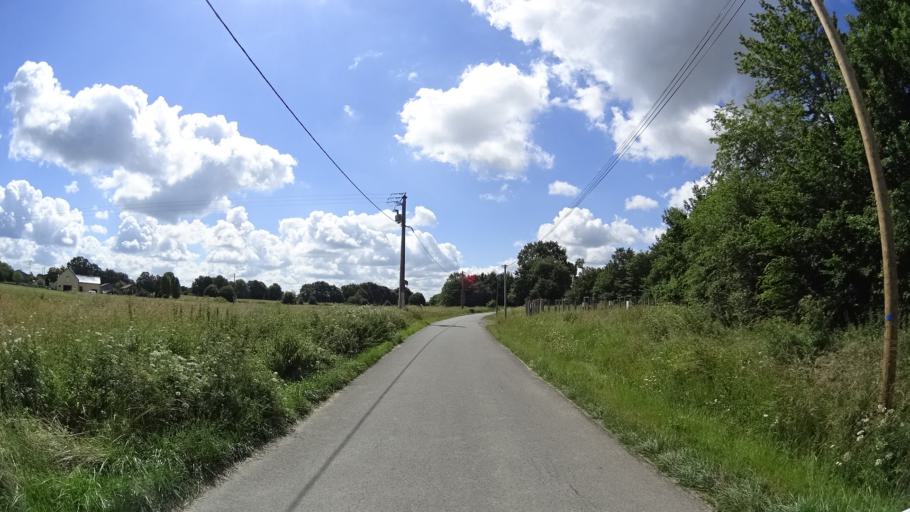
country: FR
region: Brittany
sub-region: Departement d'Ille-et-Vilaine
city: Le Rheu
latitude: 48.1149
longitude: -1.8154
